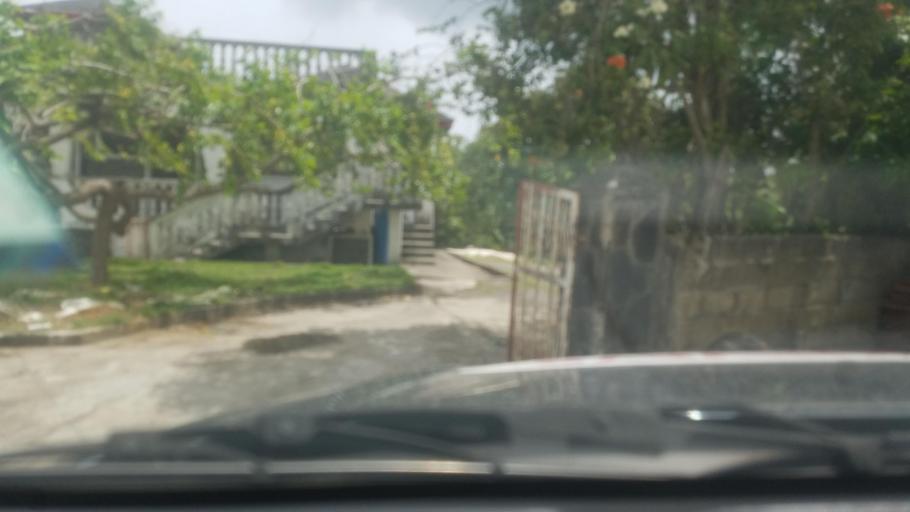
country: LC
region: Laborie Quarter
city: Laborie
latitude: 13.7499
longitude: -60.9817
